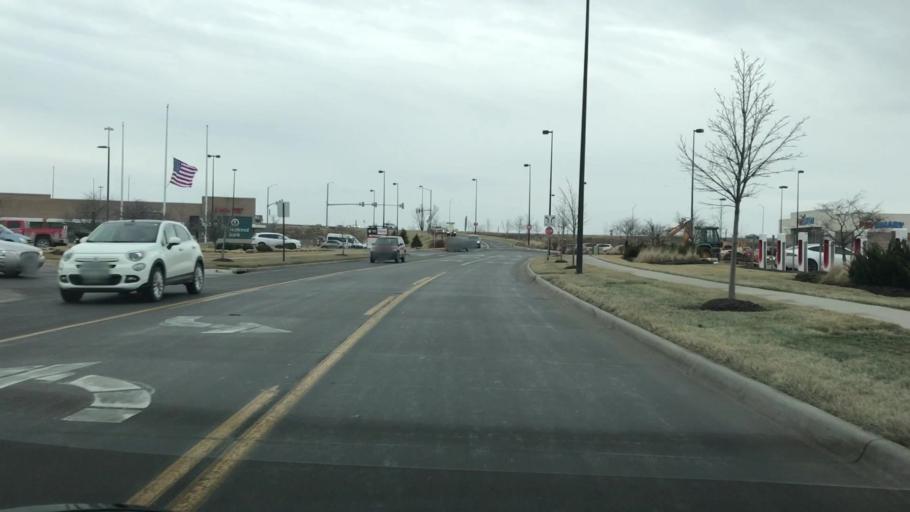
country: US
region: Iowa
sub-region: Pottawattamie County
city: Council Bluffs
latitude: 41.2213
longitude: -95.8357
